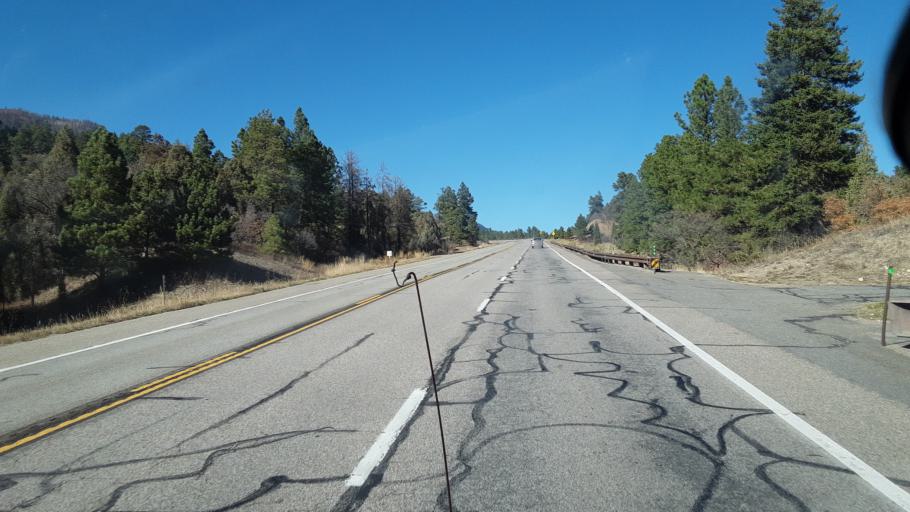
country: US
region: Colorado
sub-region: La Plata County
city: Durango
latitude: 37.4644
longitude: -107.8041
